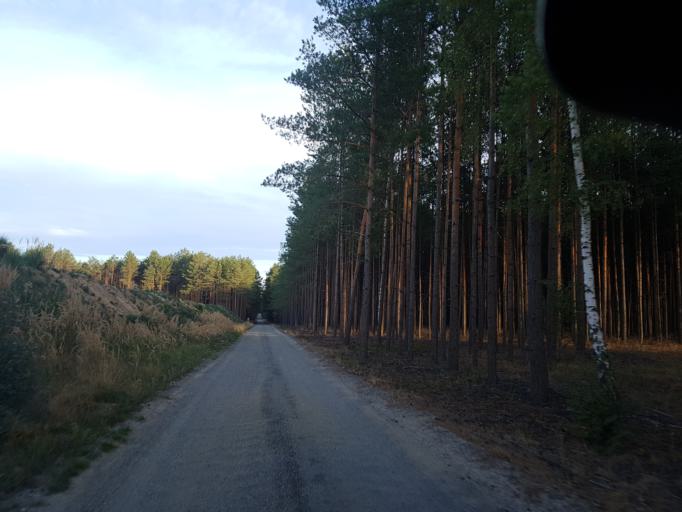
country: DE
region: Brandenburg
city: Schonewalde
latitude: 51.7394
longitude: 13.5794
